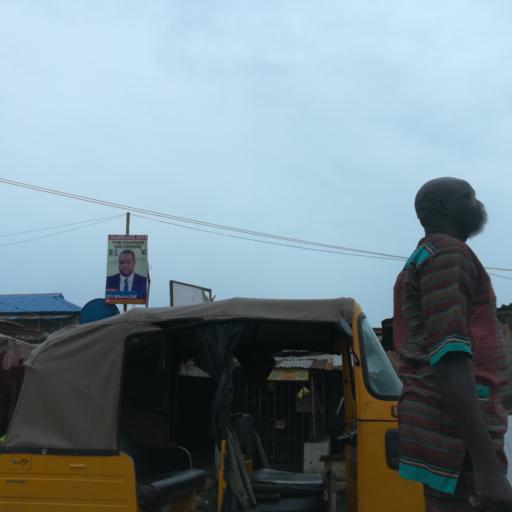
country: NG
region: Lagos
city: Makoko
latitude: 6.5004
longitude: 3.3898
